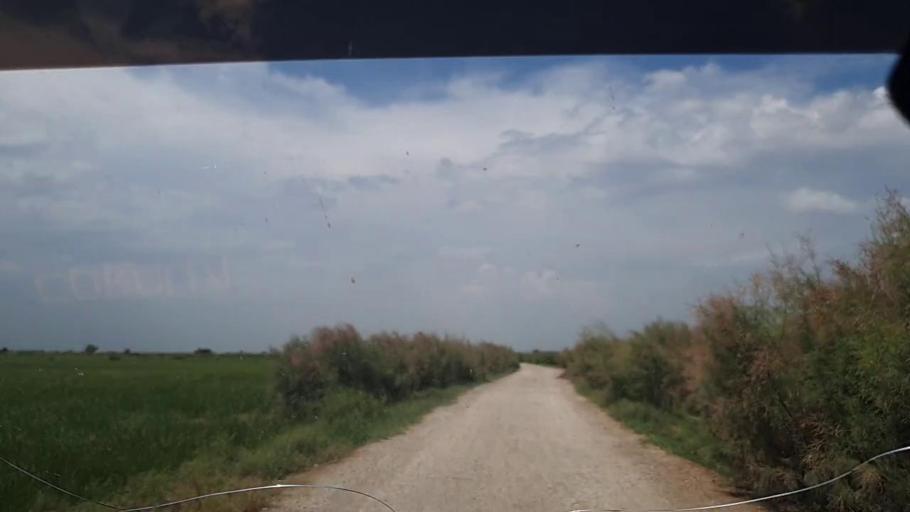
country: PK
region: Sindh
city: Ghauspur
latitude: 28.1446
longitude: 68.9819
